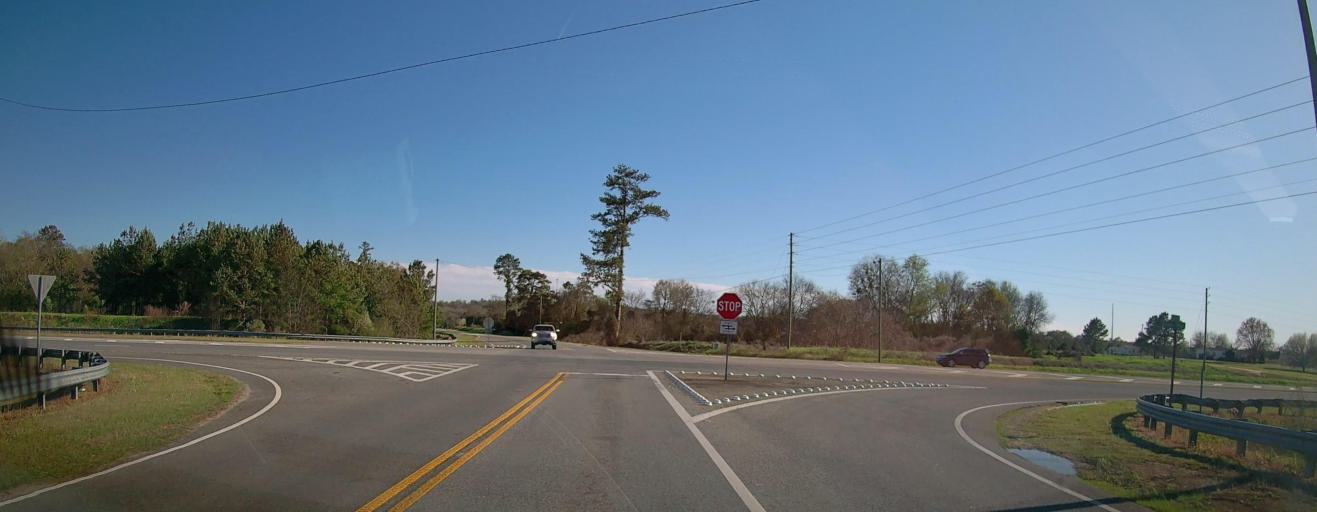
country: US
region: Georgia
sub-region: Houston County
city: Perry
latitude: 32.4306
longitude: -83.7366
